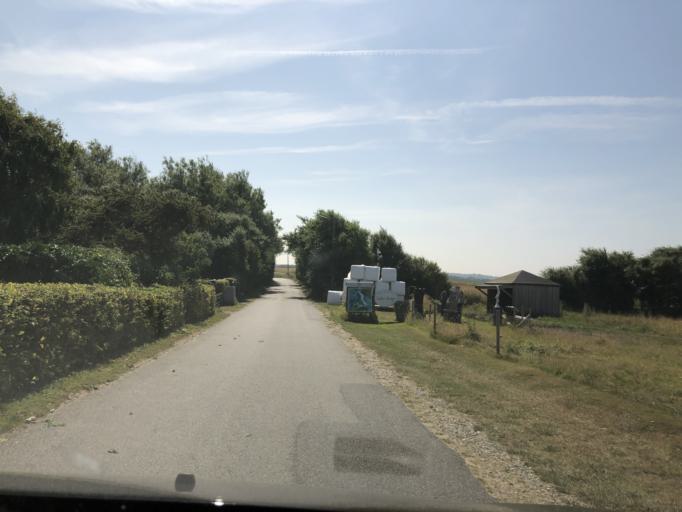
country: DK
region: South Denmark
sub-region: Faaborg-Midtfyn Kommune
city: Faaborg
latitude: 54.9493
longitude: 10.2324
